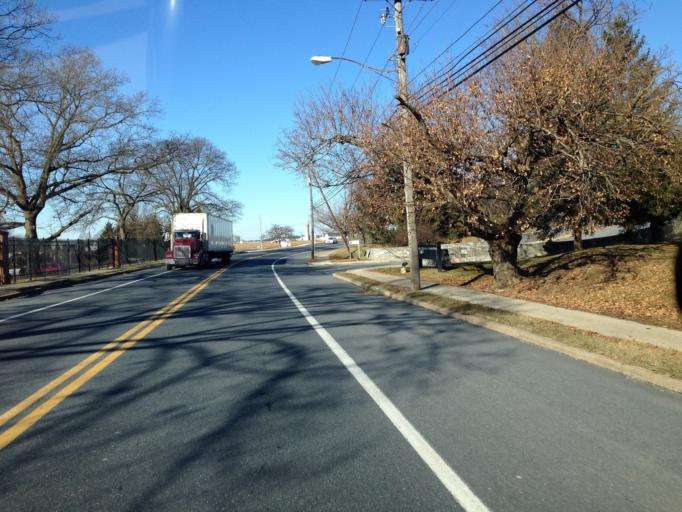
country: US
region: Pennsylvania
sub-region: Lancaster County
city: Lititz
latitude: 40.1622
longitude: -76.3154
